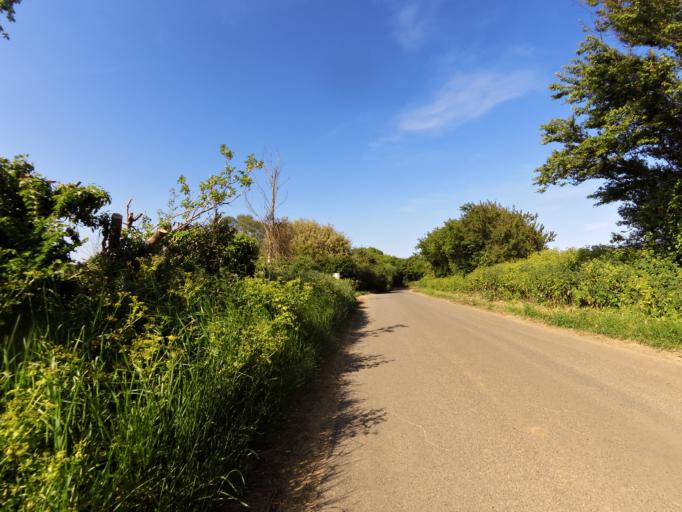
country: GB
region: England
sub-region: Suffolk
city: Felixstowe
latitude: 52.0020
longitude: 1.4171
